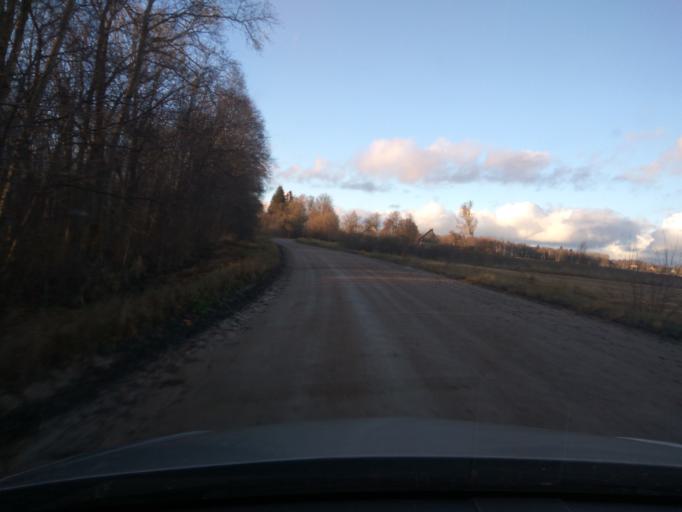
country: LV
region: Aizpute
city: Aizpute
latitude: 56.8190
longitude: 21.7760
